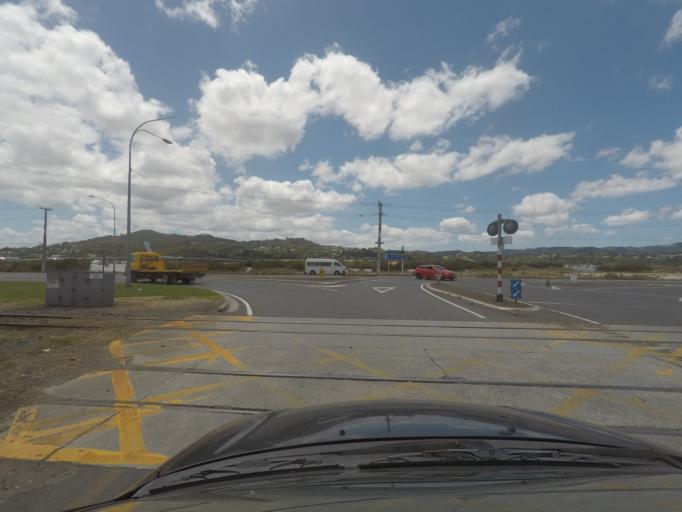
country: NZ
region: Northland
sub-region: Whangarei
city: Whangarei
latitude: -35.7390
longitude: 174.3346
